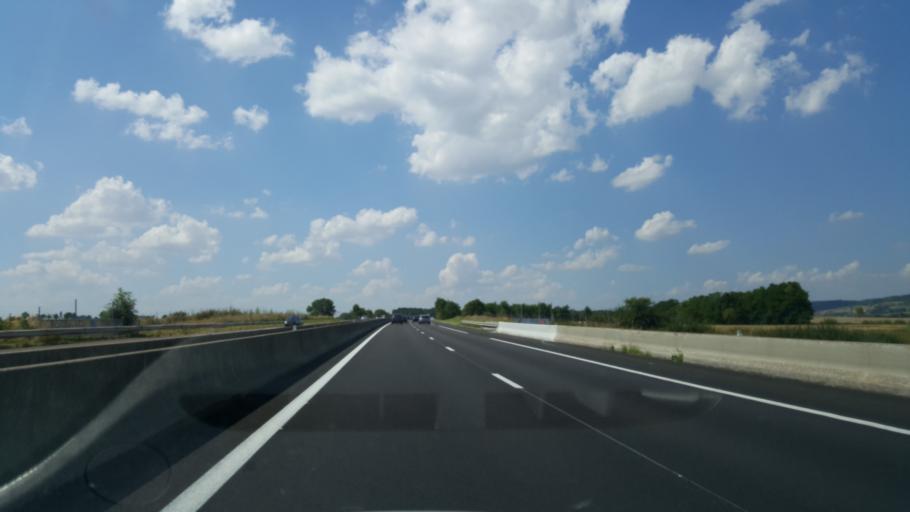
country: FR
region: Bourgogne
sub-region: Departement de la Cote-d'Or
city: Pouilly-en-Auxois
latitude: 47.2138
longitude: 4.6068
